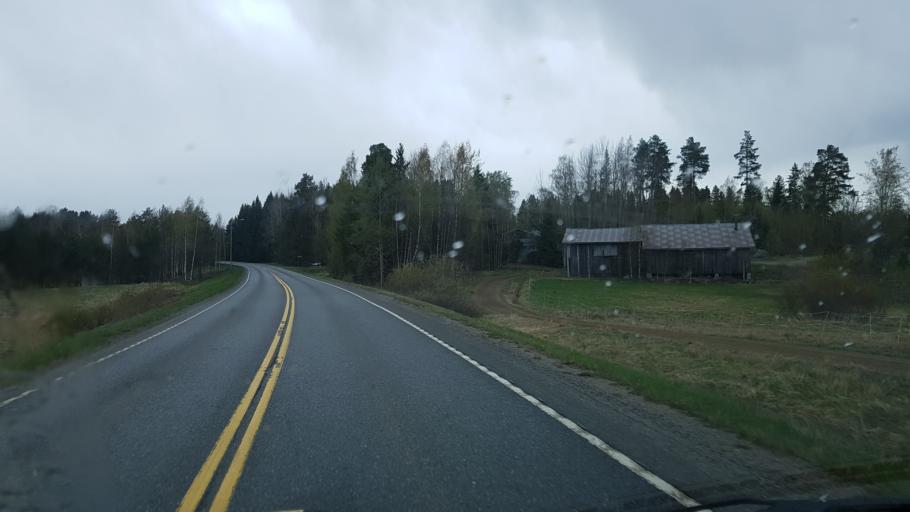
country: FI
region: Pirkanmaa
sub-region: Tampere
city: Pirkkala
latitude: 61.4262
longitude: 23.6335
